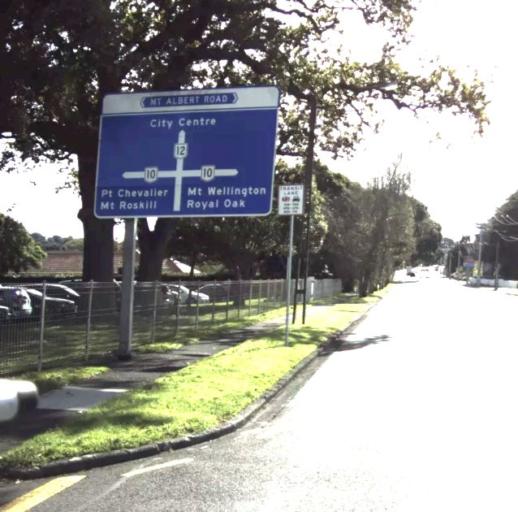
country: NZ
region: Auckland
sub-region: Auckland
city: Auckland
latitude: -36.9142
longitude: 174.7688
